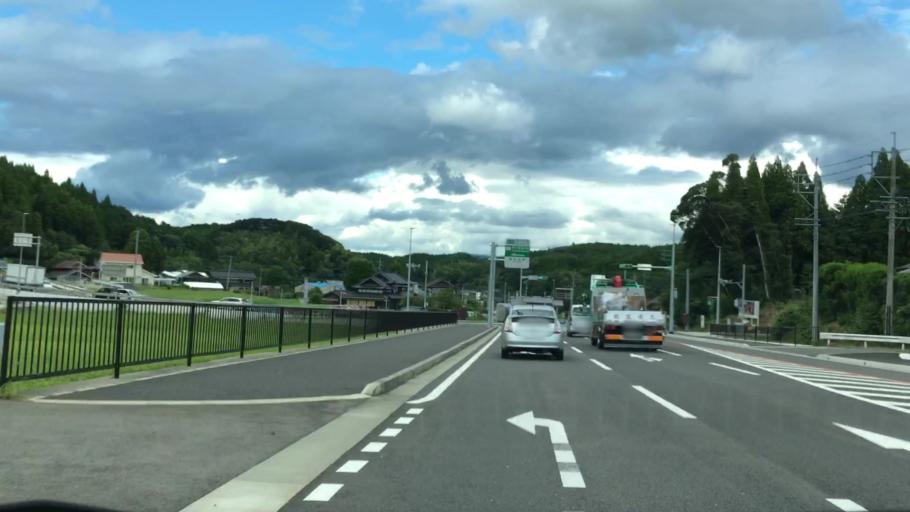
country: JP
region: Saga Prefecture
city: Imaricho-ko
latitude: 33.2937
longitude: 129.9118
